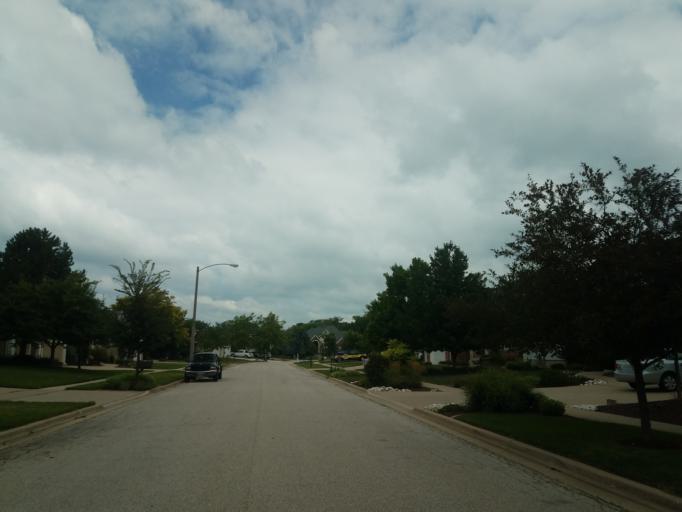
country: US
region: Illinois
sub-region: McLean County
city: Twin Grove
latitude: 40.4516
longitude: -89.0456
